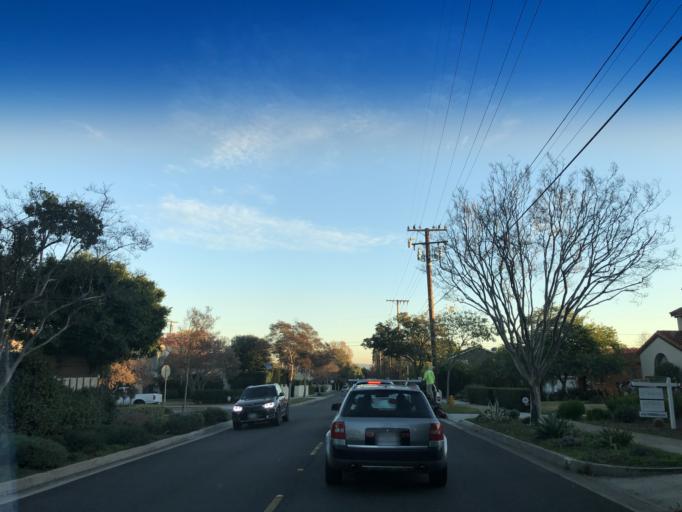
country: US
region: California
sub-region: Los Angeles County
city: South Pasadena
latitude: 34.1153
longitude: -118.1357
